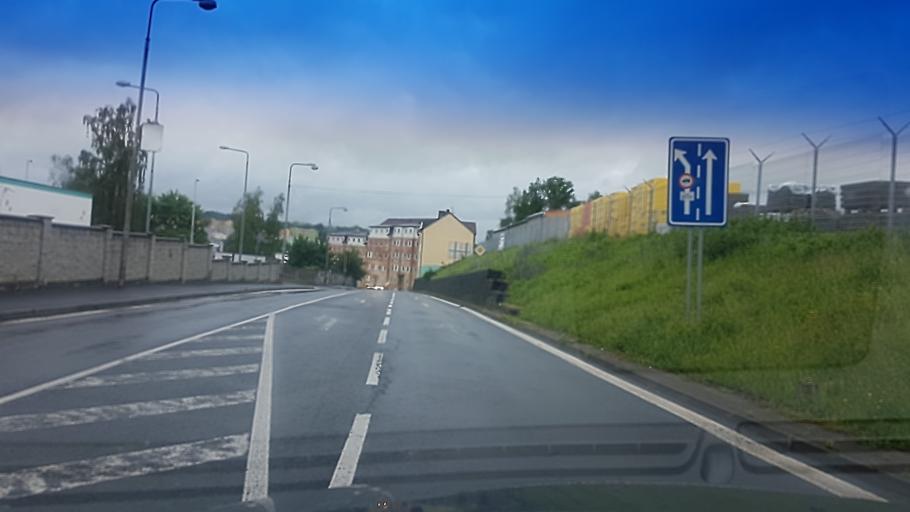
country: CZ
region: Karlovarsky
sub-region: Okres Cheb
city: Cheb
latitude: 50.0788
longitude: 12.3812
